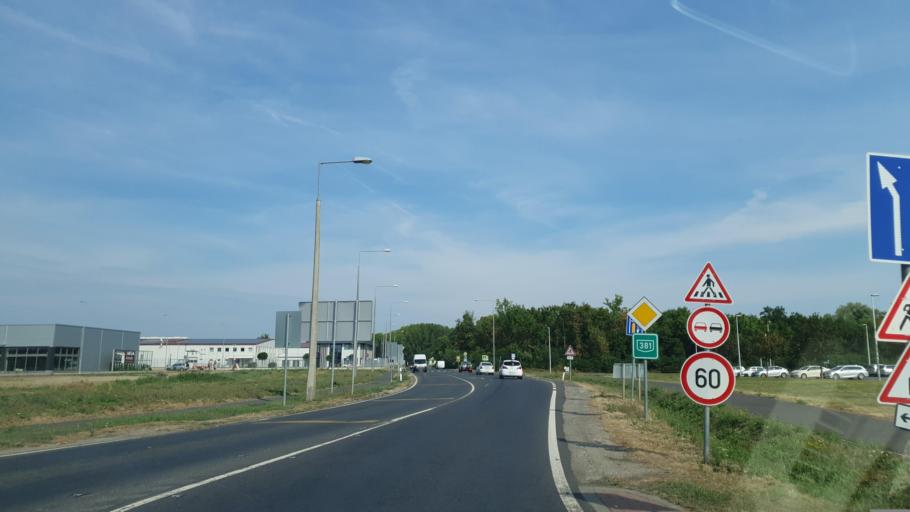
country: HU
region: Szabolcs-Szatmar-Bereg
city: Kisvarda
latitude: 48.2337
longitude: 22.0633
